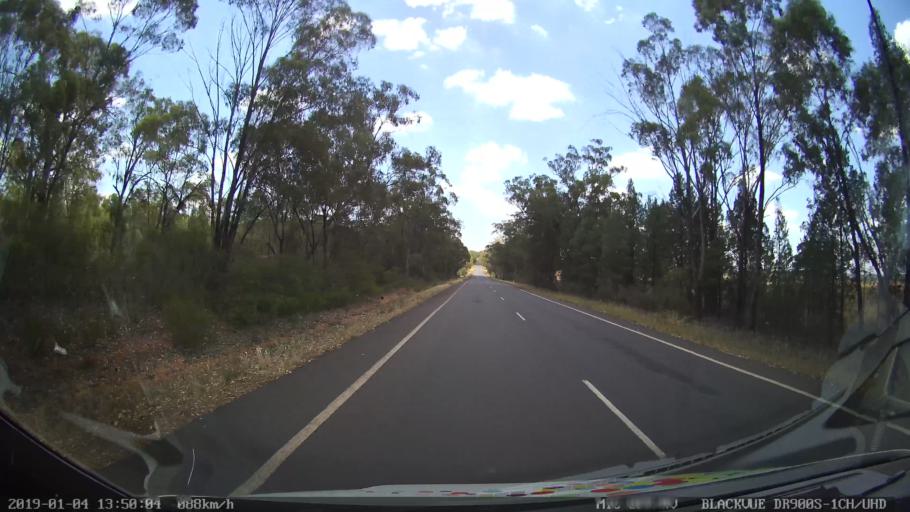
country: AU
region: New South Wales
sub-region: Dubbo Municipality
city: Dubbo
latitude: -32.4244
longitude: 148.5752
